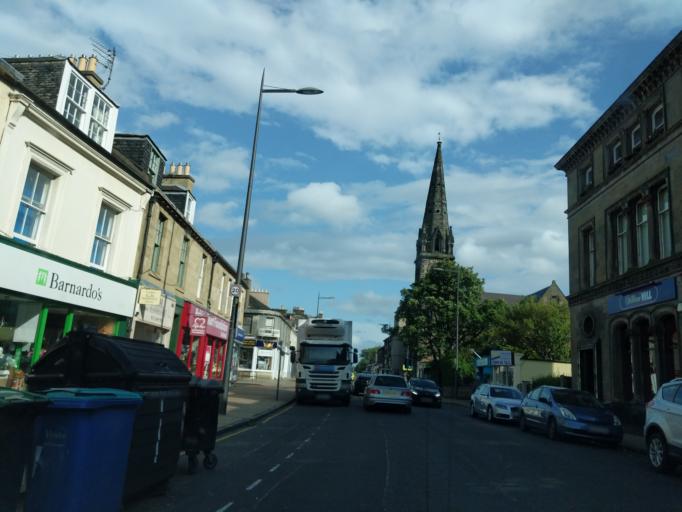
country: GB
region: Scotland
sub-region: West Lothian
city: Seafield
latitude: 55.9525
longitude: -3.1134
